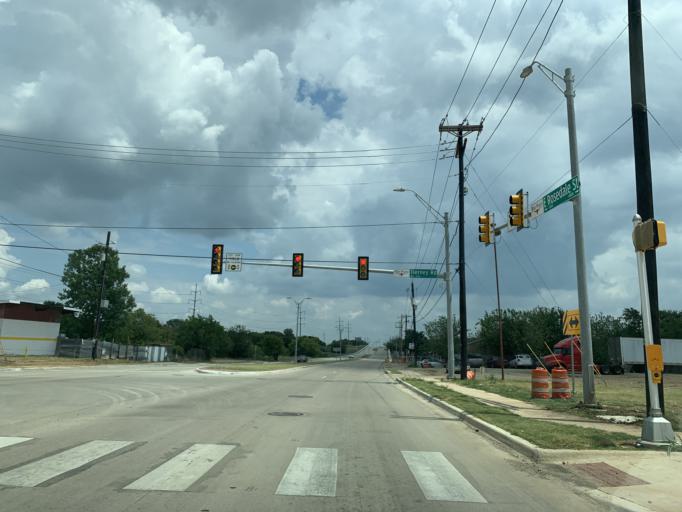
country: US
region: Texas
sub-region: Tarrant County
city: Forest Hill
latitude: 32.7311
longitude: -97.2453
